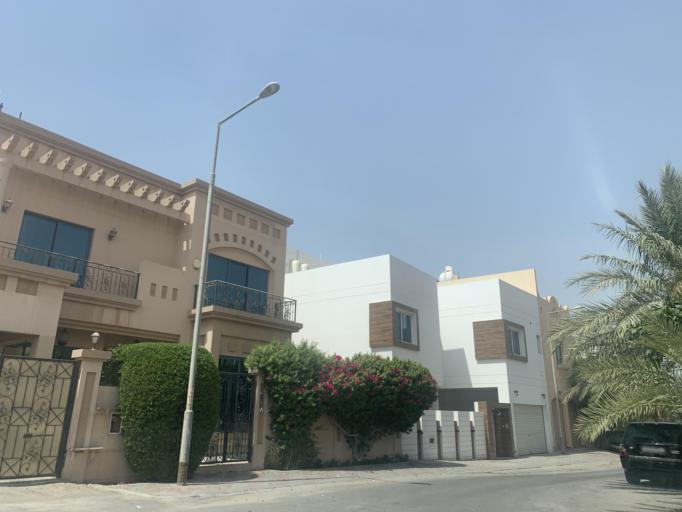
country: BH
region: Northern
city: Madinat `Isa
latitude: 26.1884
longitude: 50.4934
